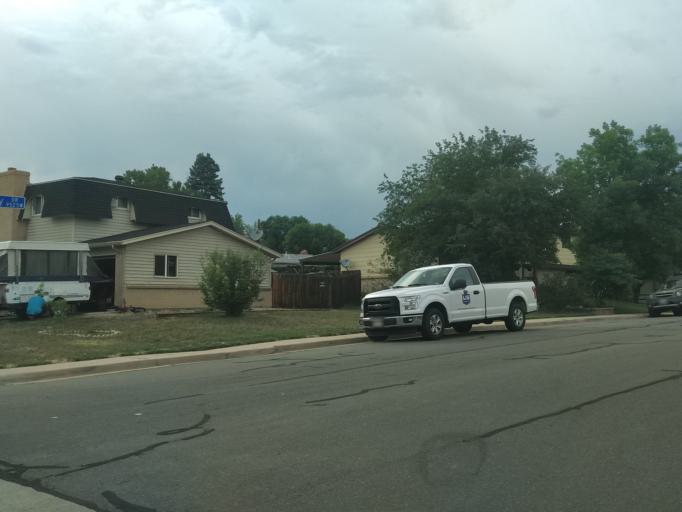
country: US
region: Colorado
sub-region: Jefferson County
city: Lakewood
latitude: 39.6967
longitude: -105.1044
